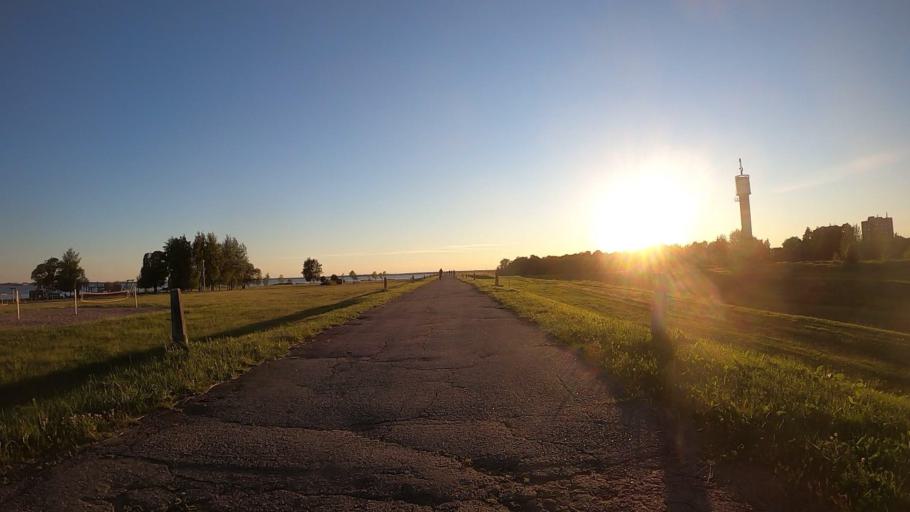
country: LV
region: Salaspils
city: Salaspils
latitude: 56.8475
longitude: 24.3440
